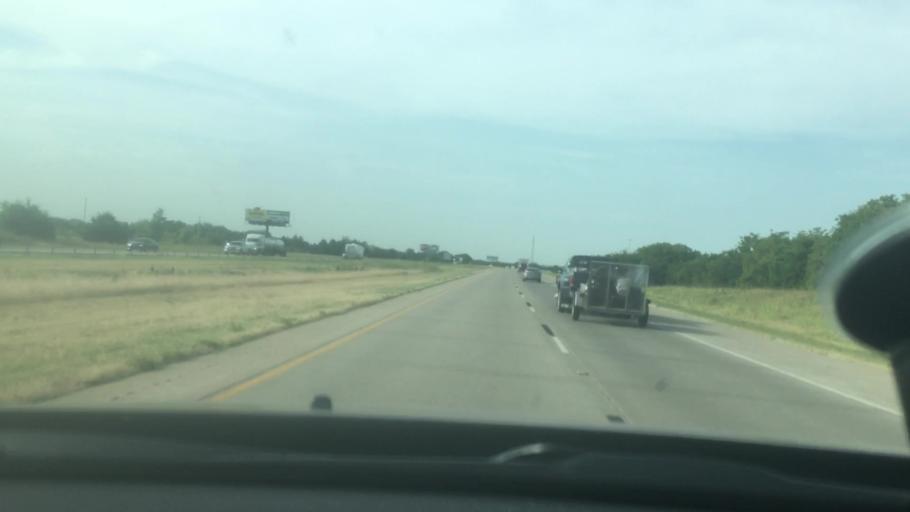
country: US
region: Oklahoma
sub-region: Carter County
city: Ardmore
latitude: 34.2910
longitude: -97.1595
